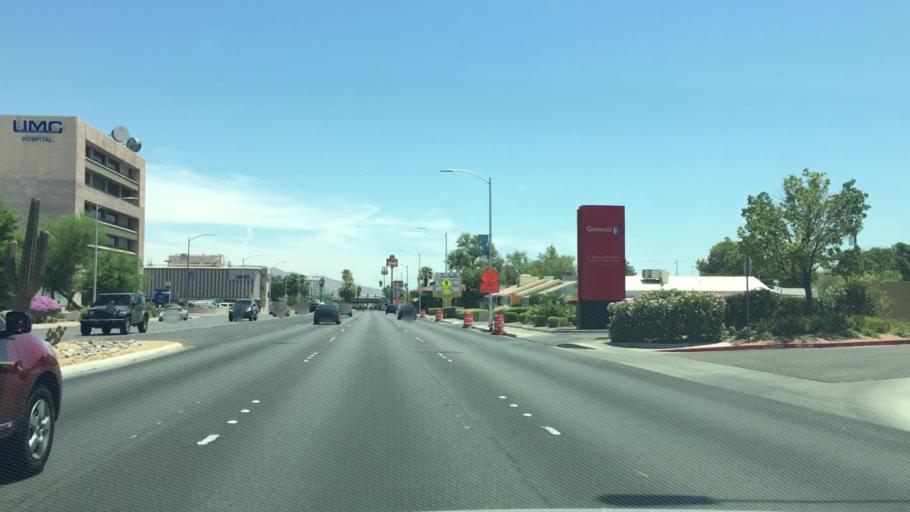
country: US
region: Nevada
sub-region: Clark County
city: Las Vegas
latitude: 36.1588
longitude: -115.1699
